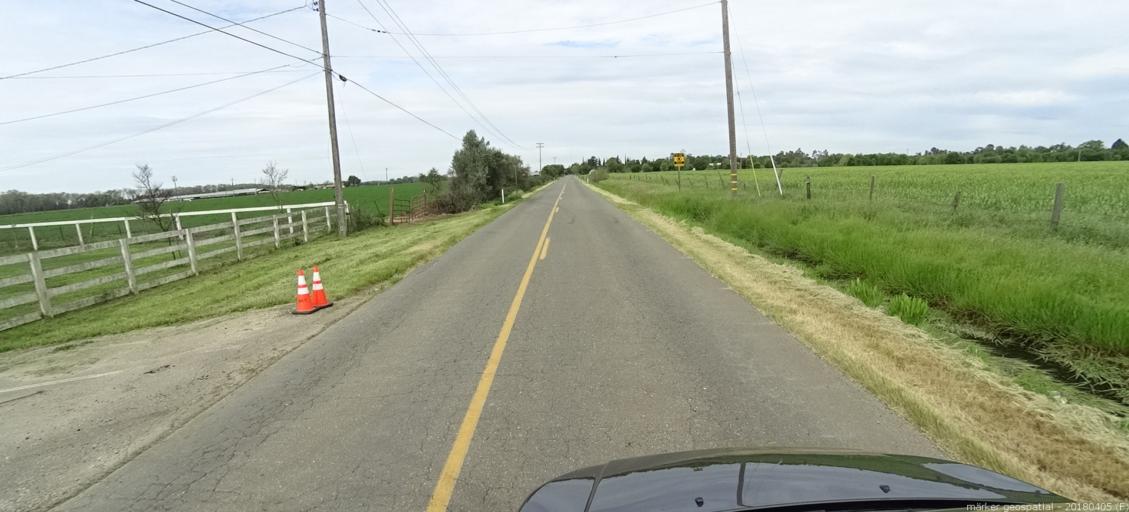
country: US
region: California
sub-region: Sacramento County
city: Galt
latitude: 38.2402
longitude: -121.3139
